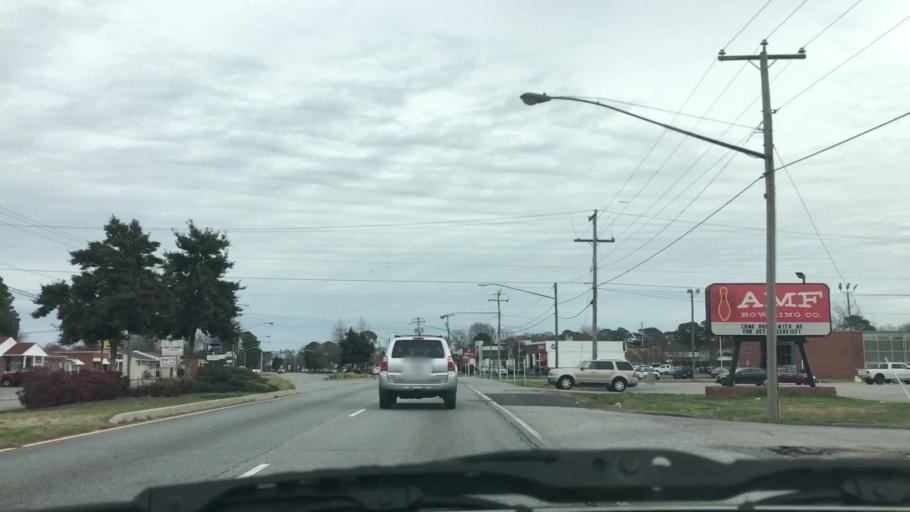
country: US
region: Virginia
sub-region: City of Norfolk
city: Norfolk
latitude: 36.9151
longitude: -76.2149
